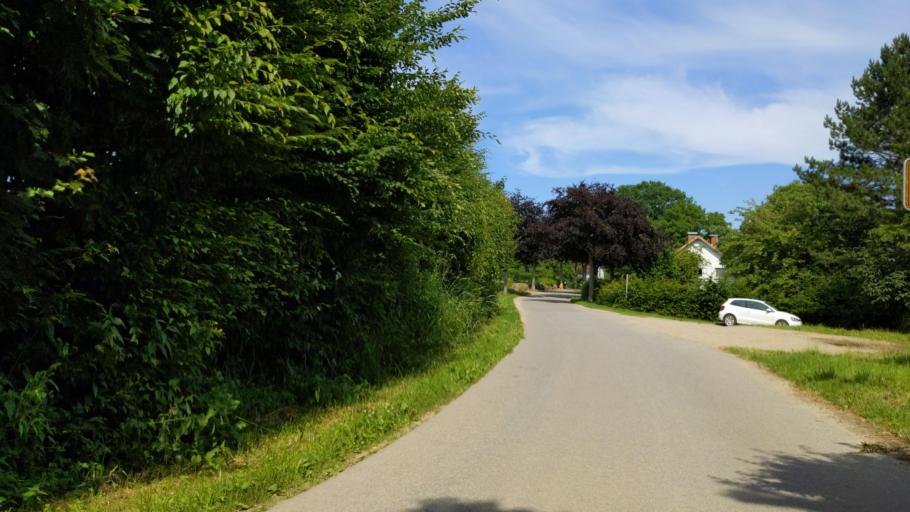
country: DE
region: Schleswig-Holstein
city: Eutin
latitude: 54.1060
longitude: 10.6036
